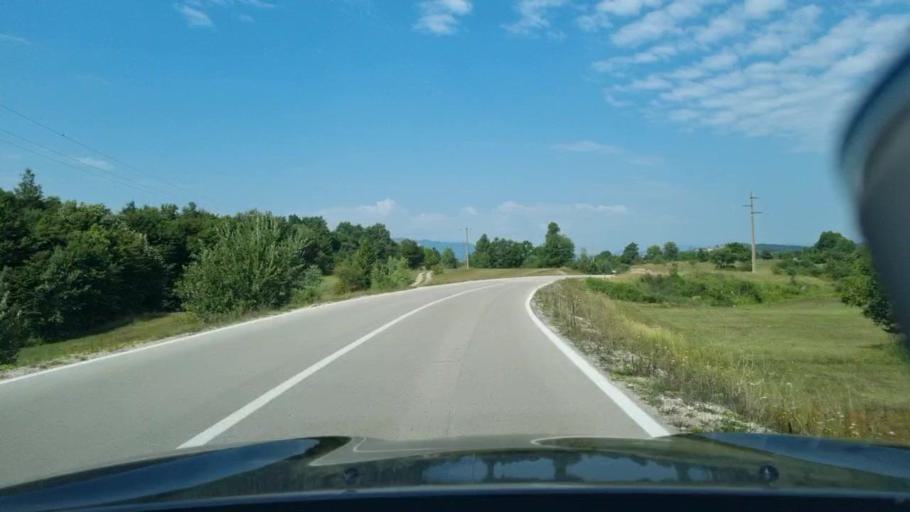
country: BA
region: Federation of Bosnia and Herzegovina
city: Ostrozac
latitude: 44.8856
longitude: 15.9317
